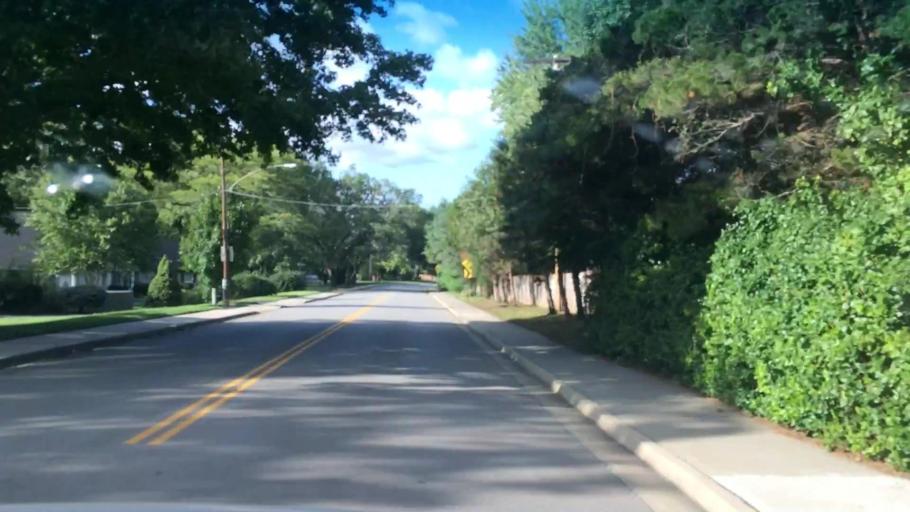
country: US
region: Kansas
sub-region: Johnson County
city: Fairway
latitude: 39.0242
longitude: -94.6303
